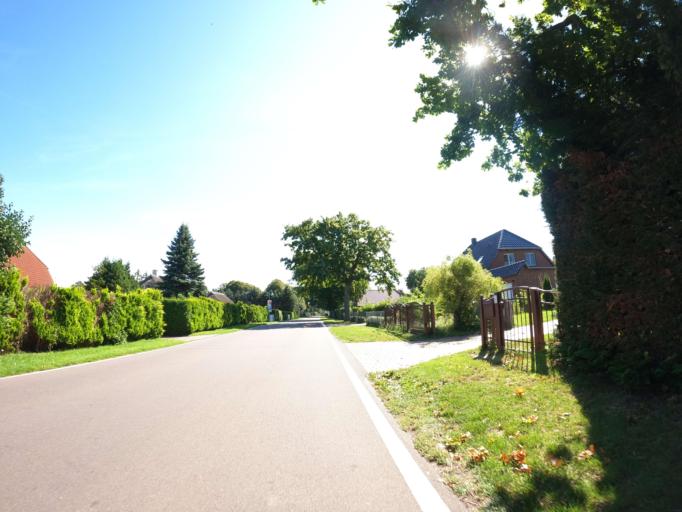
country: DE
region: Mecklenburg-Vorpommern
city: Prohn
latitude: 54.4149
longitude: 13.0141
